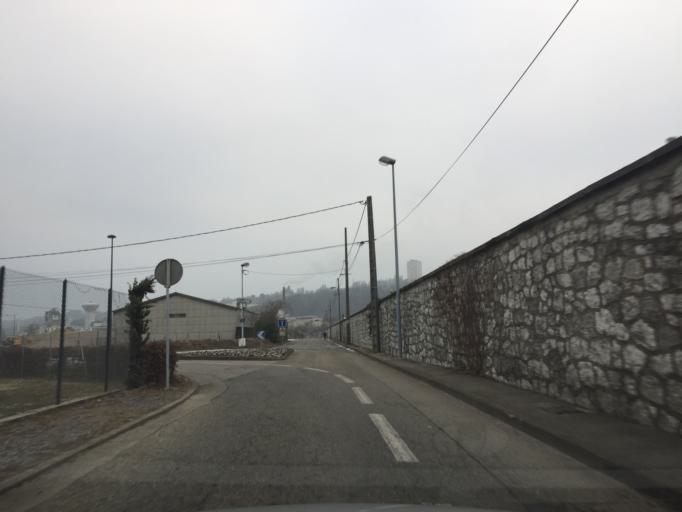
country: FR
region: Rhone-Alpes
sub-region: Departement de la Savoie
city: Cognin
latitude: 45.5777
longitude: 5.9053
